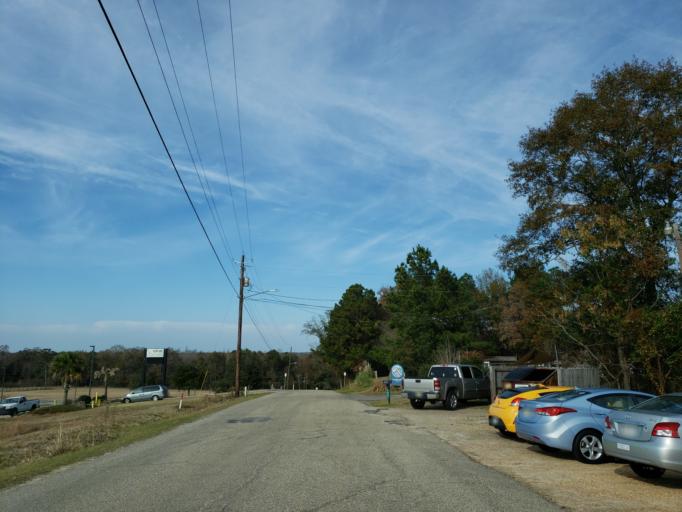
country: US
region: Mississippi
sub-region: Forrest County
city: Glendale
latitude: 31.3517
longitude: -89.3352
